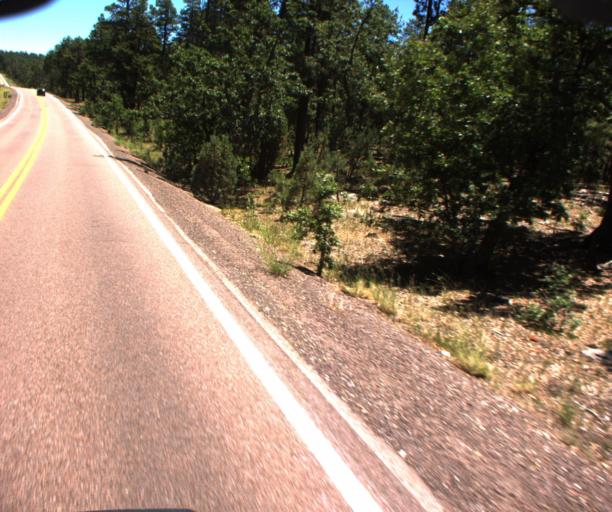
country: US
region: Arizona
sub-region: Gila County
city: Pine
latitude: 34.4404
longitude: -111.4805
